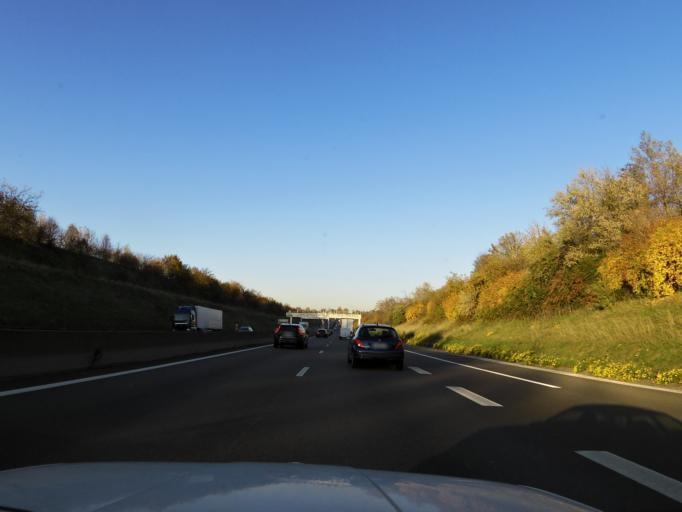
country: FR
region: Rhone-Alpes
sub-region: Departement du Rhone
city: Chassieu
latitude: 45.7355
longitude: 4.9818
